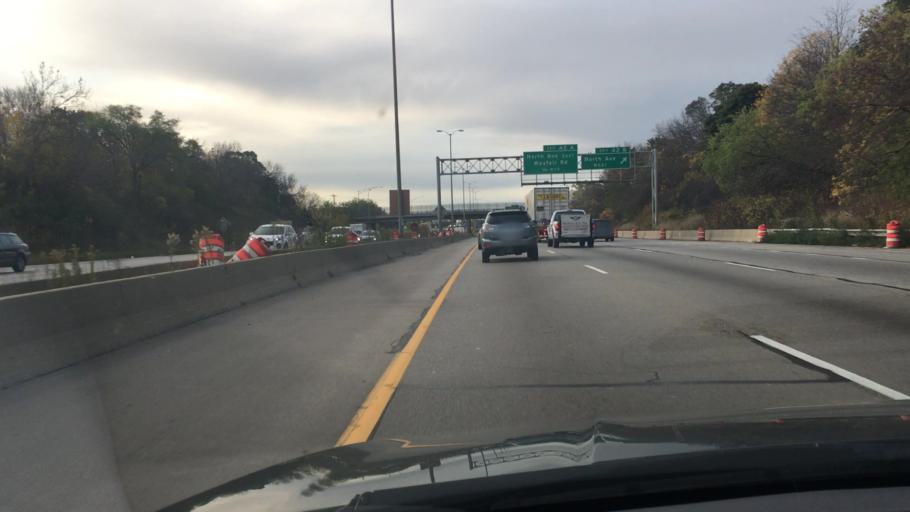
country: US
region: Wisconsin
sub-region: Waukesha County
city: Elm Grove
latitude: 43.0646
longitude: -88.0534
